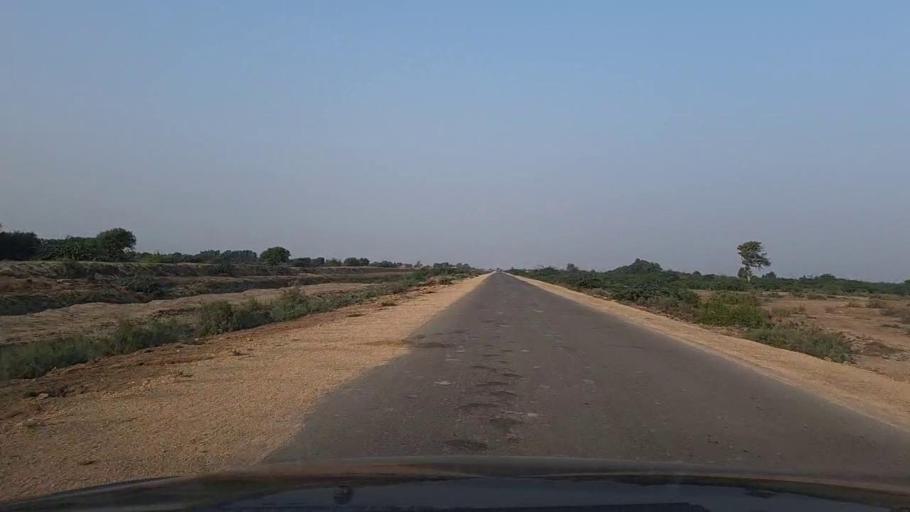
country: PK
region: Sindh
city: Mirpur Sakro
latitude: 24.4782
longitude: 67.8037
